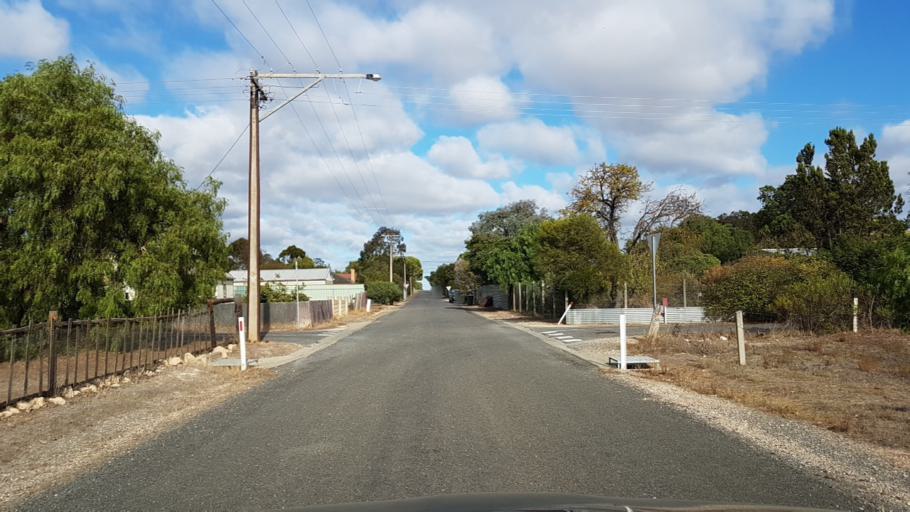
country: AU
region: South Australia
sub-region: Alexandrina
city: Langhorne Creek
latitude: -35.4033
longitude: 138.9734
